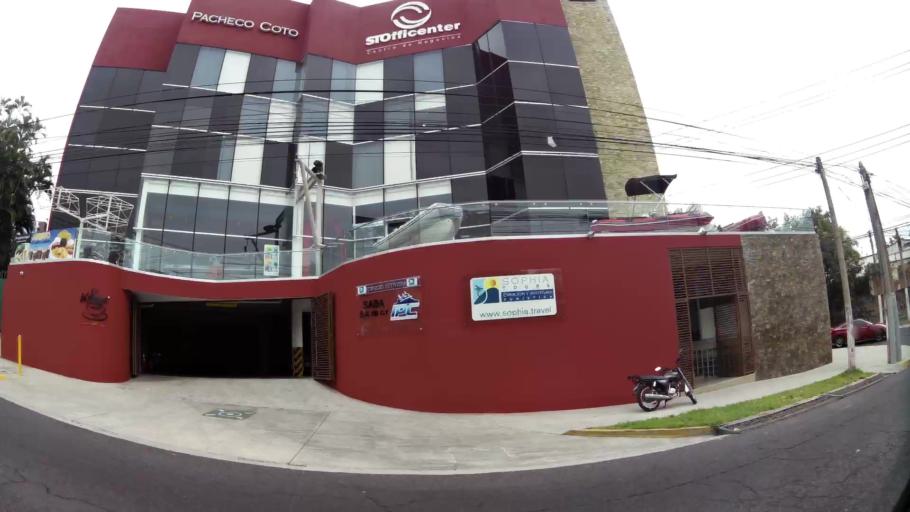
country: SV
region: San Salvador
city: Mejicanos
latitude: 13.7095
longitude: -89.2441
